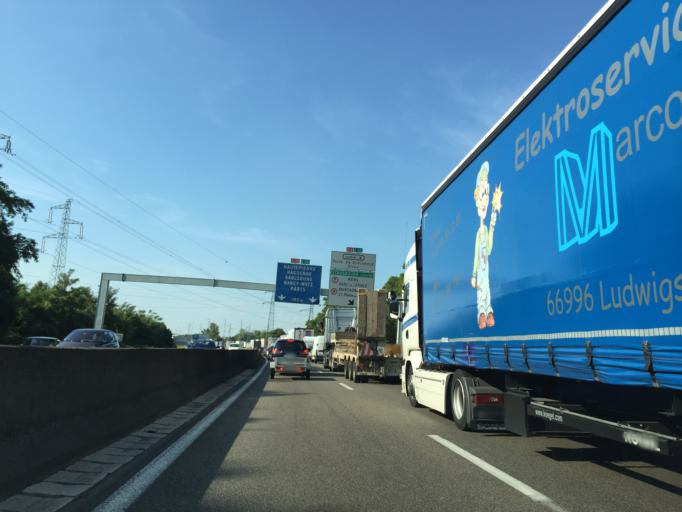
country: FR
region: Alsace
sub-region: Departement du Bas-Rhin
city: Strasbourg
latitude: 48.5618
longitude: 7.7334
